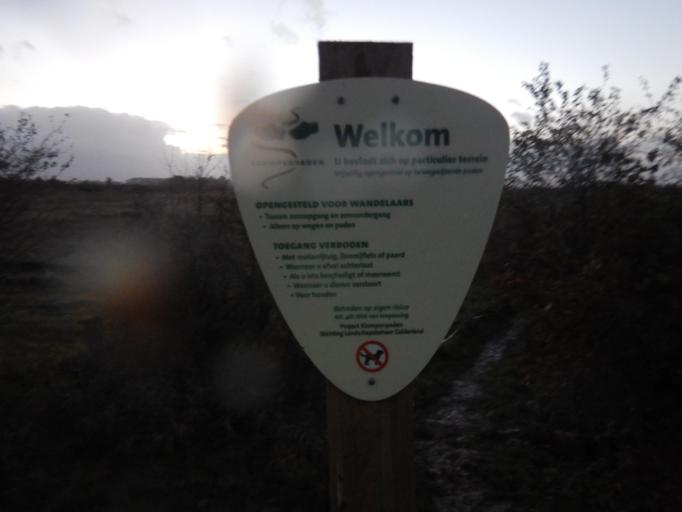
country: NL
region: Gelderland
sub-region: Gemeente Zevenaar
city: Zevenaar
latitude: 51.9114
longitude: 6.0716
